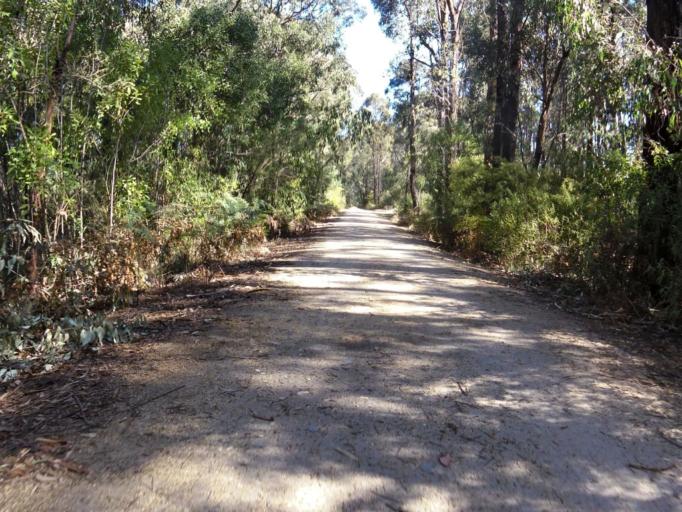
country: AU
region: Victoria
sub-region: Latrobe
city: Moe
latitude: -38.3819
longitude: 146.1924
